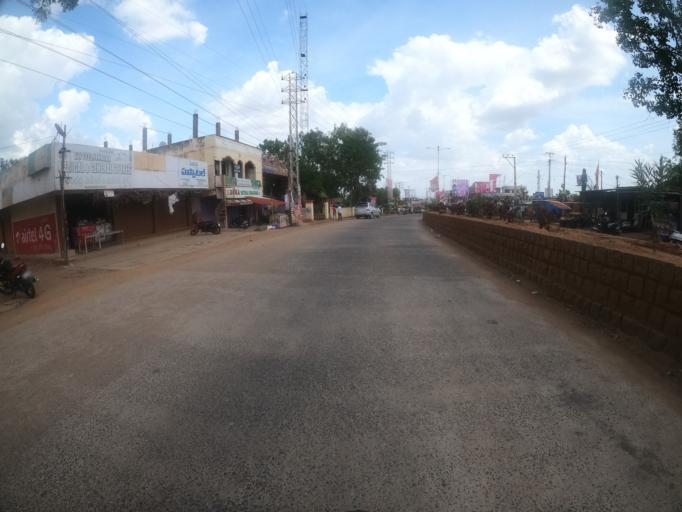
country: IN
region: Telangana
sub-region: Rangareddi
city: Sriramnagar
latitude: 17.3143
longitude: 78.1390
